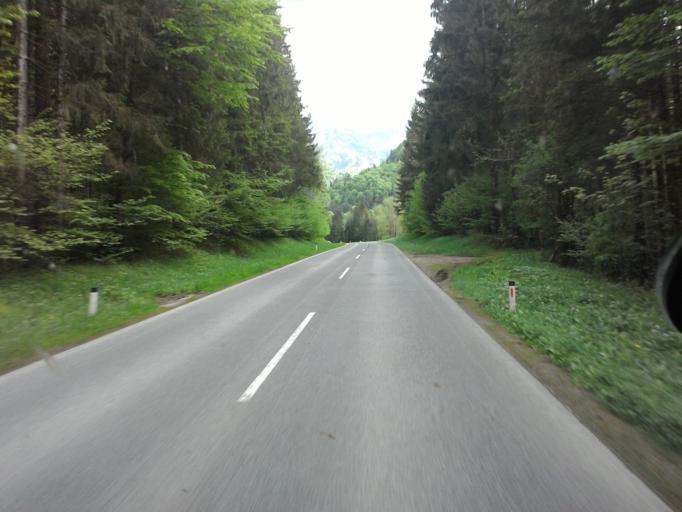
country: AT
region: Styria
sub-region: Politischer Bezirk Liezen
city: Landl
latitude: 47.6787
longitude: 14.7091
